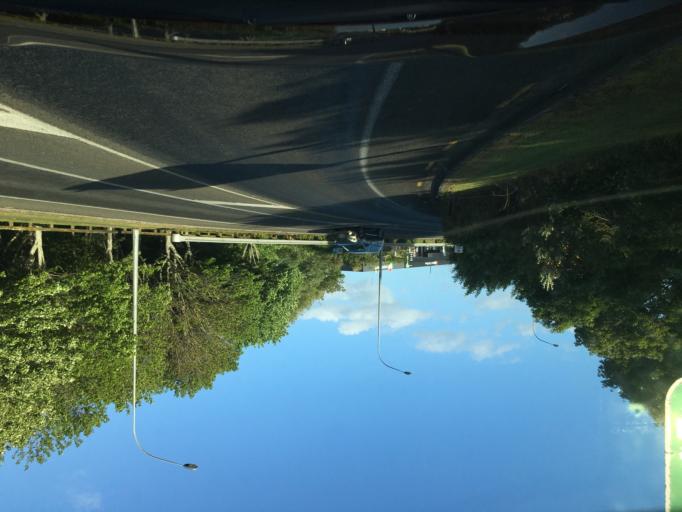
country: NZ
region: Waikato
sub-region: Waipa District
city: Cambridge
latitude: -38.0086
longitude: 175.3303
